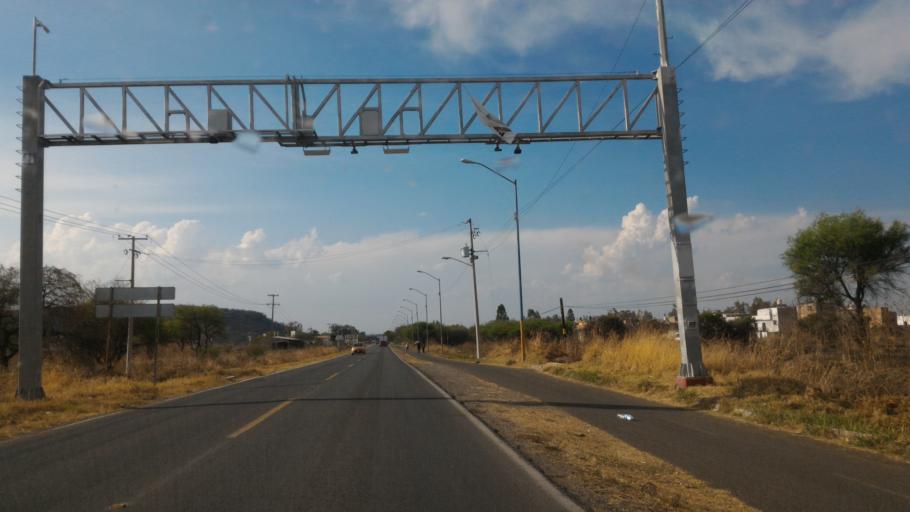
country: MX
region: Guanajuato
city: Ciudad Manuel Doblado
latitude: 20.7390
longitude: -101.9544
